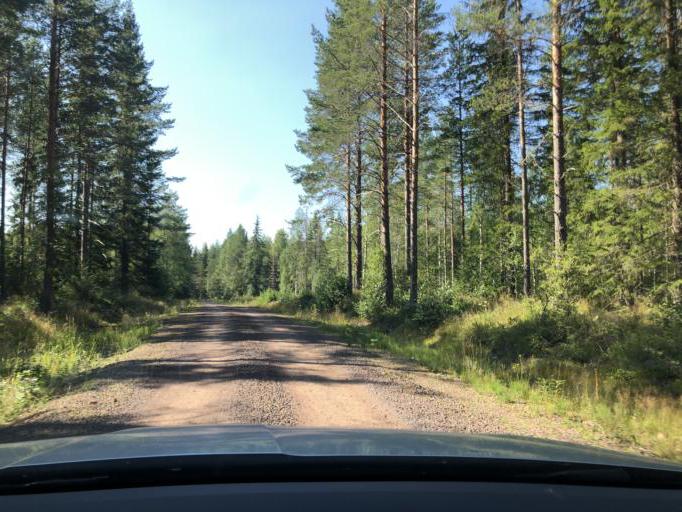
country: SE
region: Dalarna
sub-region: Orsa Kommun
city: Orsa
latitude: 61.2203
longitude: 14.7168
